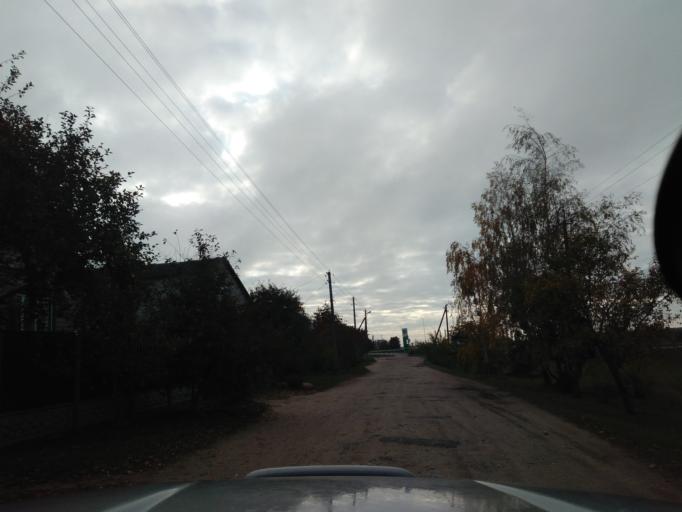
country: BY
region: Minsk
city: Kapyl'
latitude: 53.1508
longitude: 27.0727
